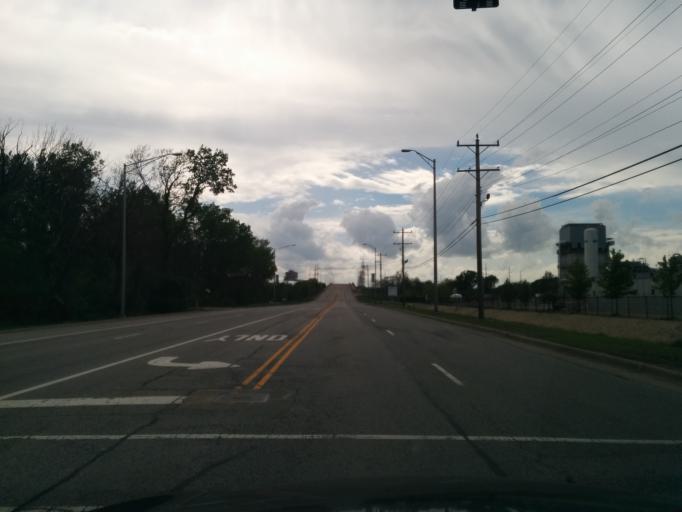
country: US
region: Illinois
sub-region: Will County
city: Romeoville
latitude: 41.6408
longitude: -88.0531
